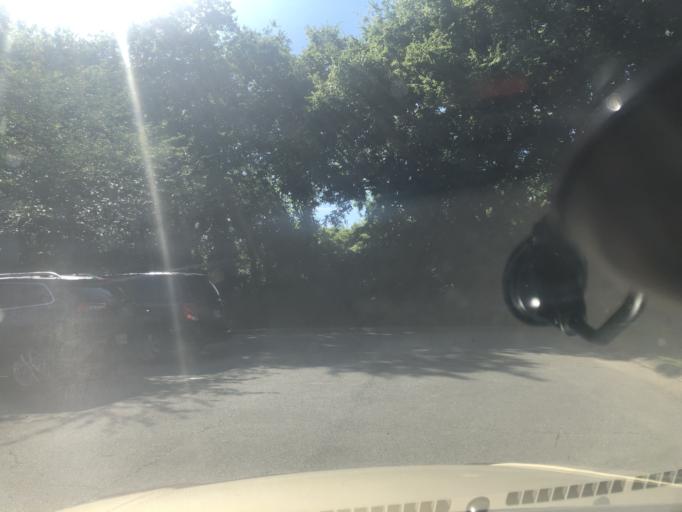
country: US
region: Tennessee
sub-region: Davidson County
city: Lakewood
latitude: 36.2424
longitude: -86.6712
